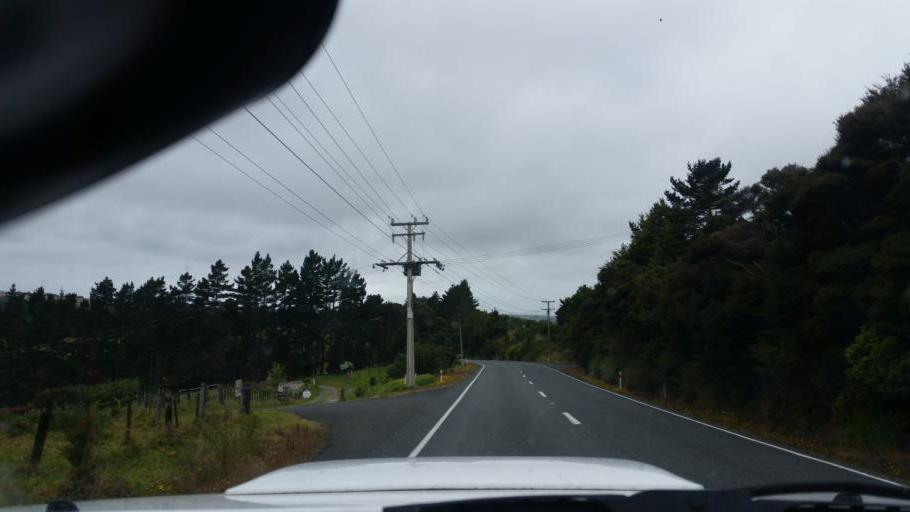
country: NZ
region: Auckland
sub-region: Auckland
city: Wellsford
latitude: -36.1324
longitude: 174.5423
